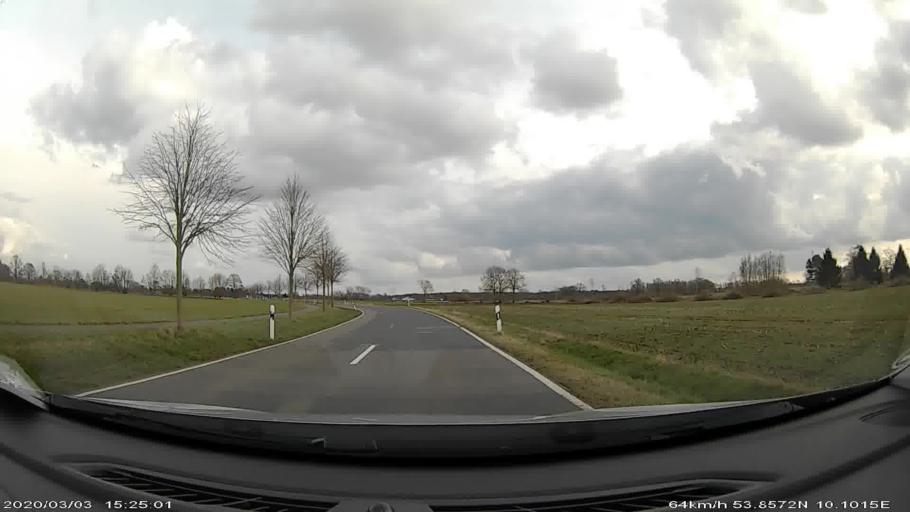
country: DE
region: Schleswig-Holstein
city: Sievershutten
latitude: 53.8572
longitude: 10.1004
